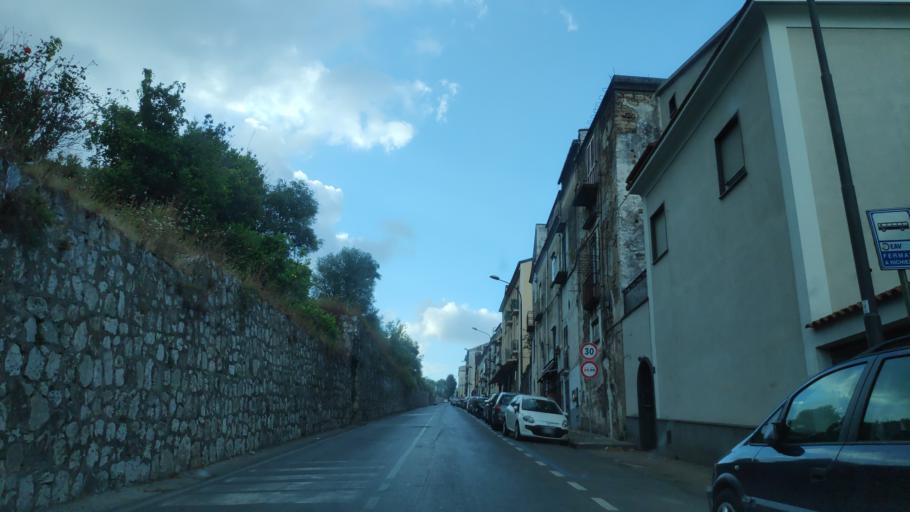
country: IT
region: Campania
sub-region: Provincia di Napoli
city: Piano di Sorrento
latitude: 40.6332
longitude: 14.4182
